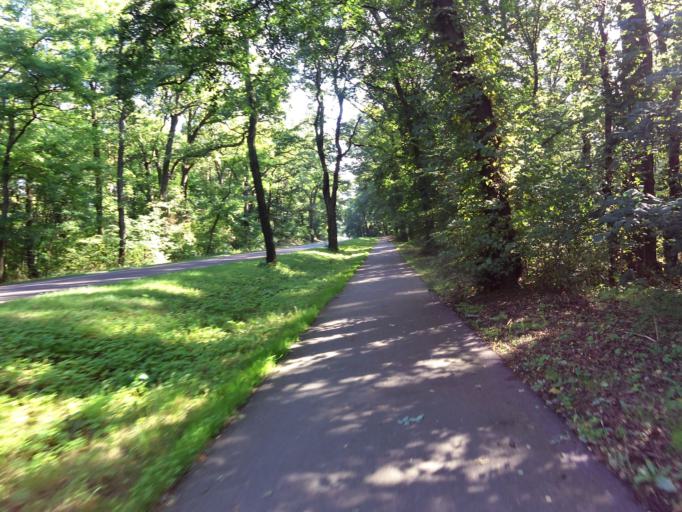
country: DE
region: Saxony-Anhalt
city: Coswig
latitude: 51.8824
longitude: 12.4951
